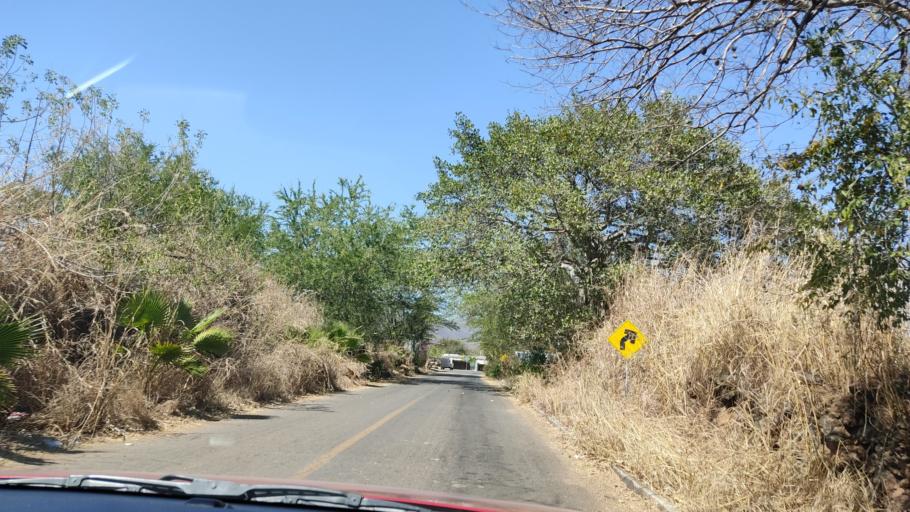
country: MX
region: Nayarit
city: Santa Maria del Oro
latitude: 21.4990
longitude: -104.6218
